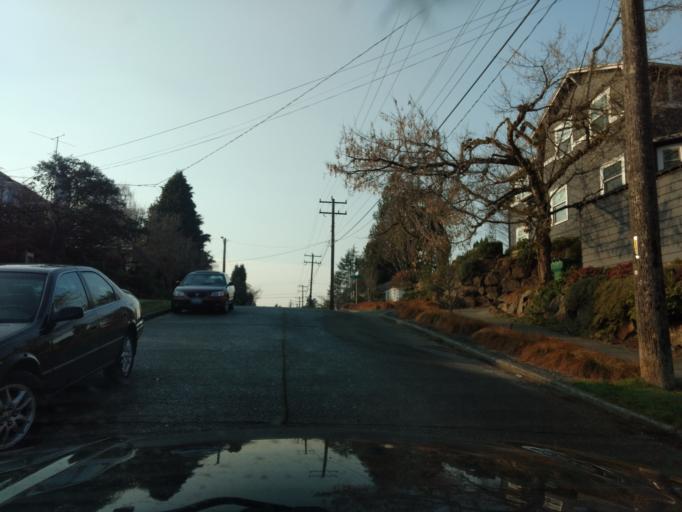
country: US
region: Washington
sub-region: King County
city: Lake Forest Park
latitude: 47.6849
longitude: -122.3048
